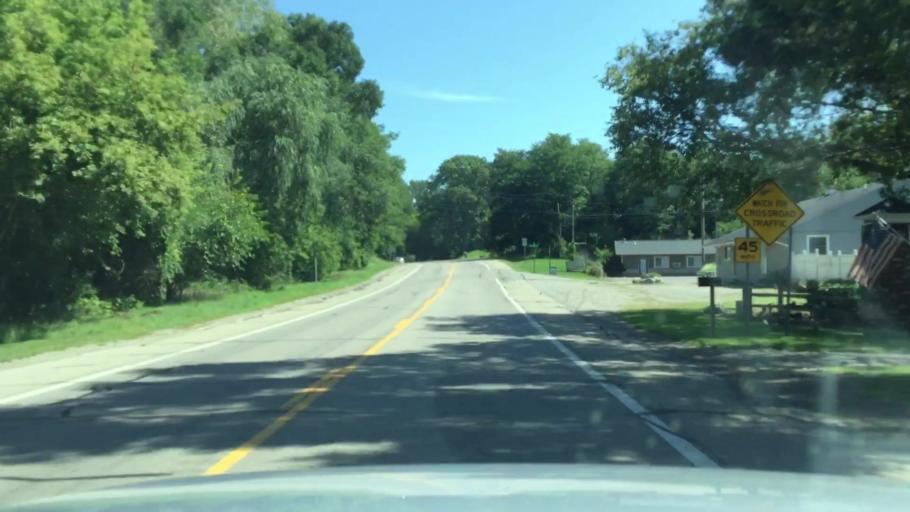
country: US
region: Michigan
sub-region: Washtenaw County
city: Manchester
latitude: 42.0635
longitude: -84.1123
